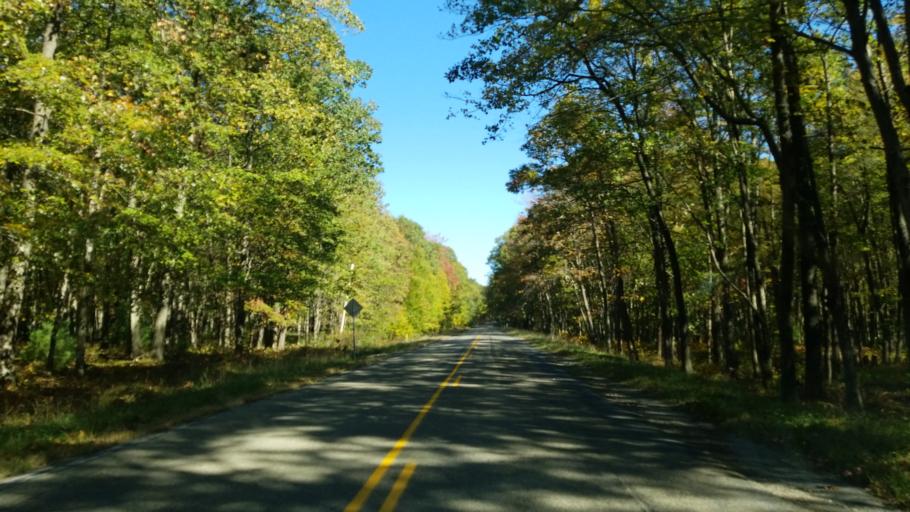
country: US
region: Pennsylvania
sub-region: Clearfield County
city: Shiloh
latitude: 41.2542
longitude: -78.3644
